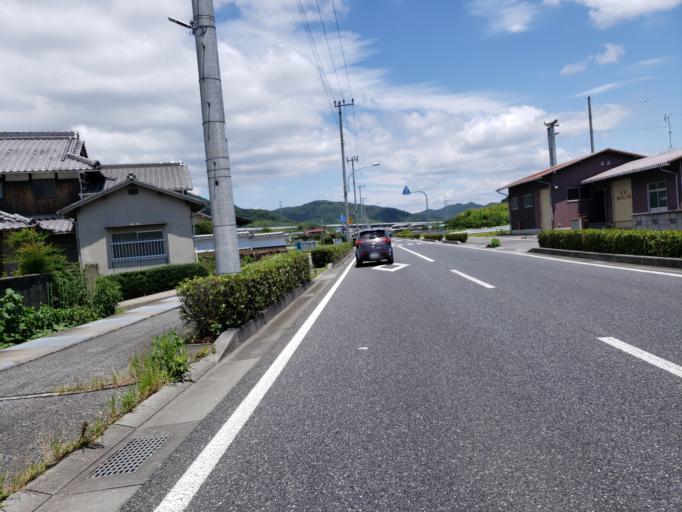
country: JP
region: Hyogo
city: Himeji
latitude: 34.8422
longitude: 134.7452
